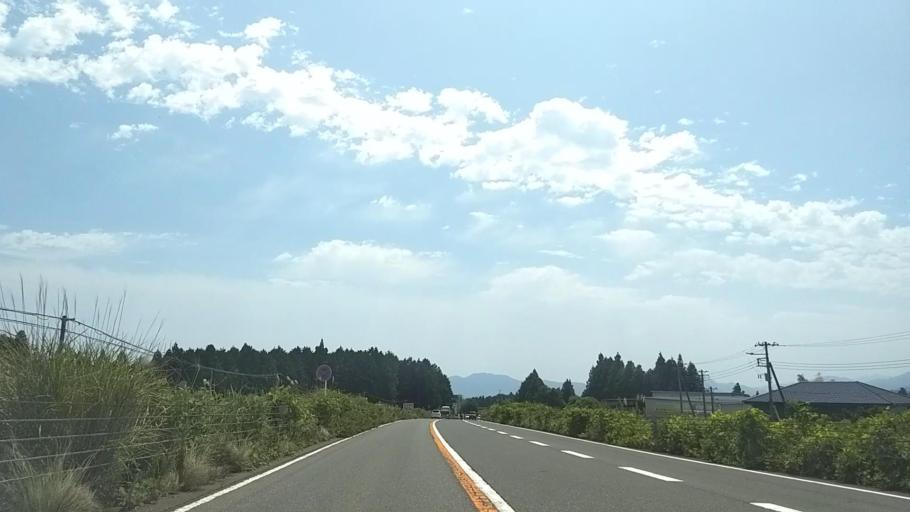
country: JP
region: Shizuoka
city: Fujinomiya
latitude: 35.2823
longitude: 138.6127
